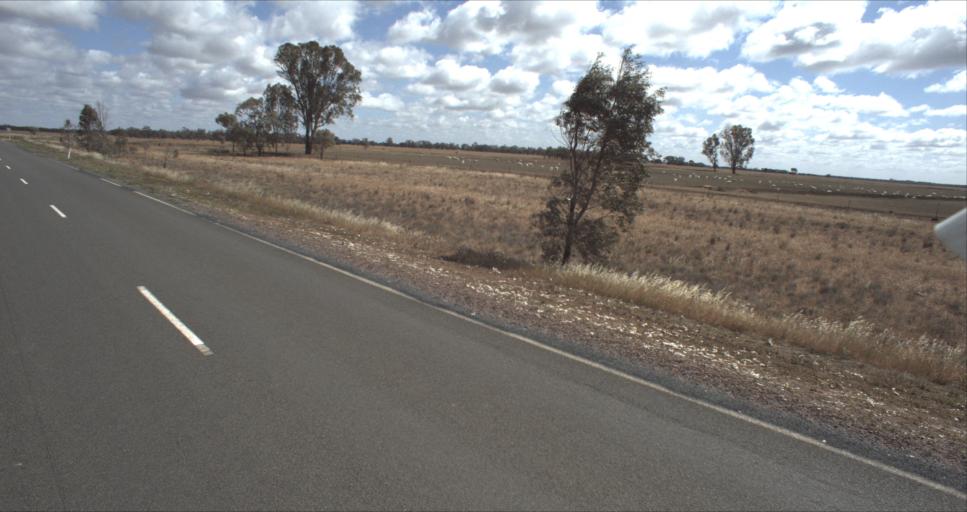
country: AU
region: New South Wales
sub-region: Murrumbidgee Shire
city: Darlington Point
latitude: -34.5818
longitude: 146.1121
